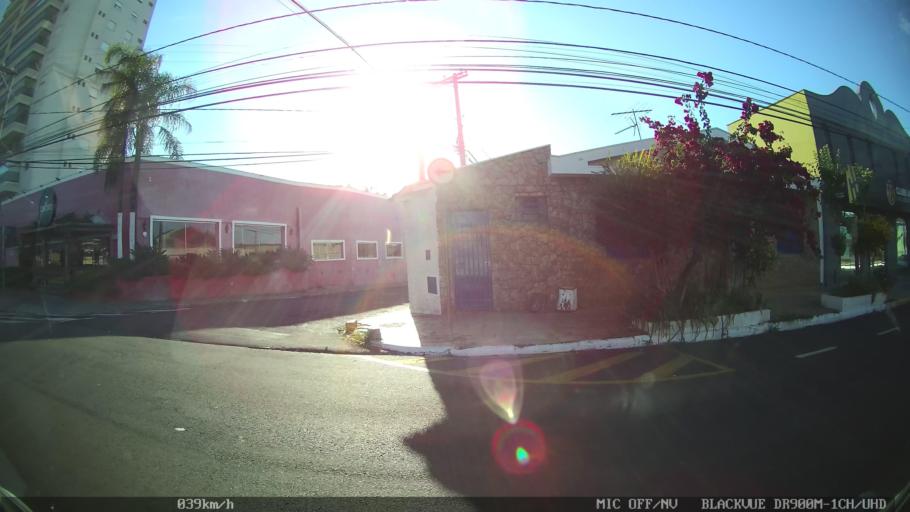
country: BR
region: Sao Paulo
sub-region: Franca
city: Franca
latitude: -20.5253
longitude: -47.3895
